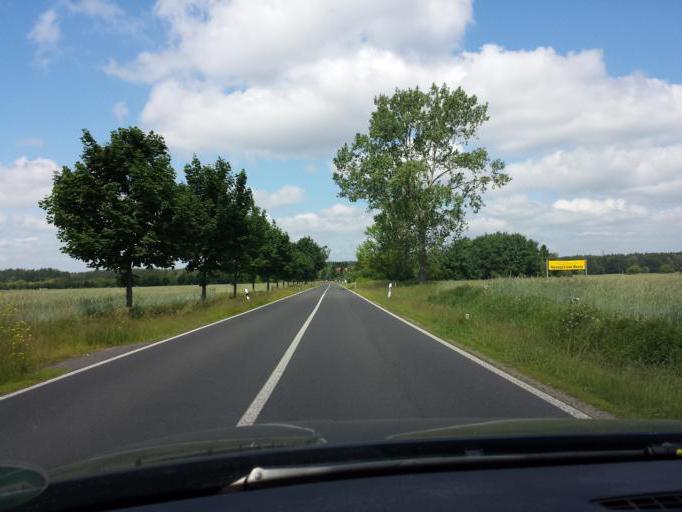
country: DE
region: Brandenburg
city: Kremmen
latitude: 52.8025
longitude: 13.0782
